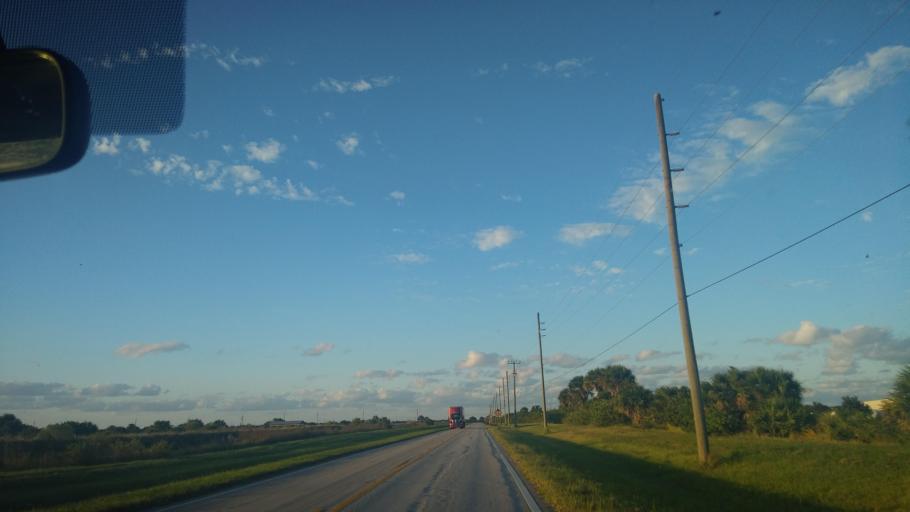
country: US
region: Florida
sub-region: Indian River County
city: Fellsmere
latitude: 27.7347
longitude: -80.6423
